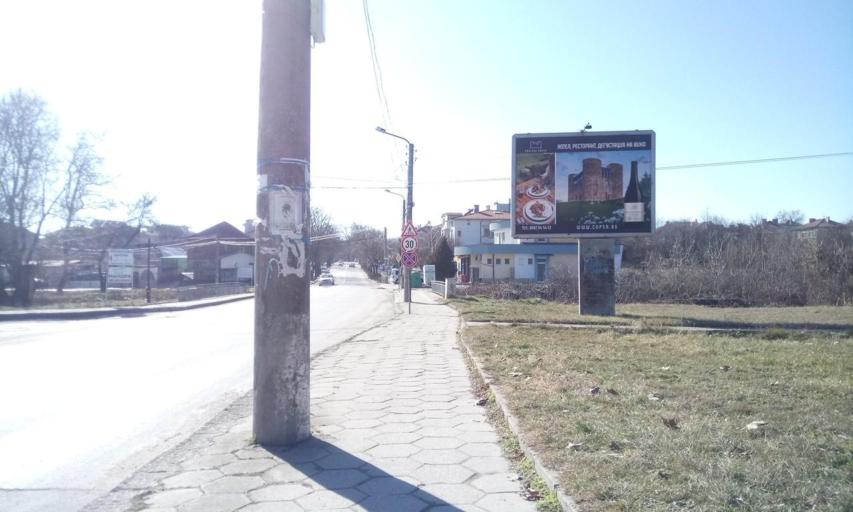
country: BG
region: Plovdiv
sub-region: Obshtina Khisarya
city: Khisarya
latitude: 42.5088
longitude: 24.7139
